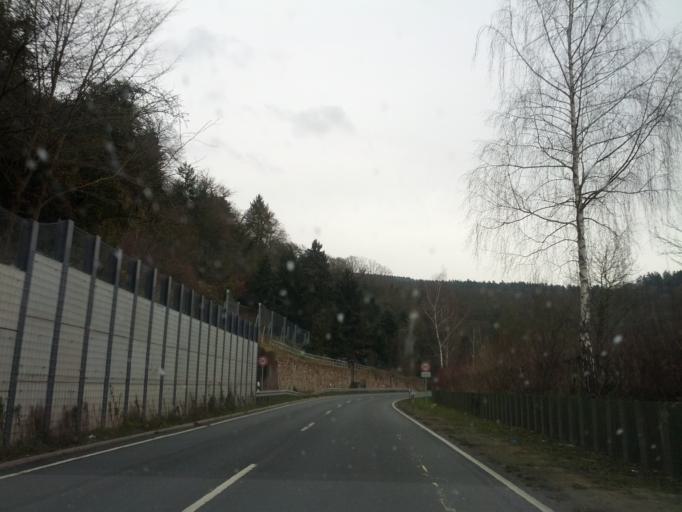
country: DE
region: Hesse
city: Witzenhausen
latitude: 51.3489
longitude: 9.8636
